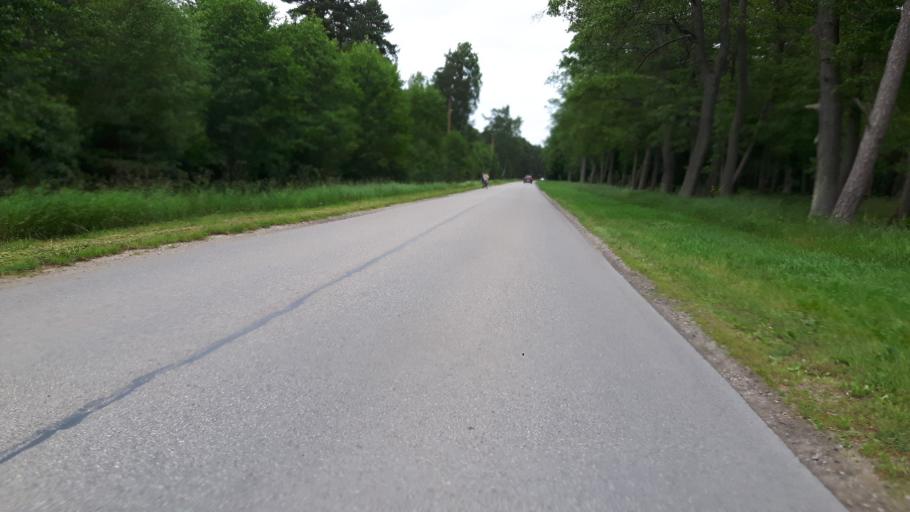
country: LV
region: Liepaja
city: Vec-Liepaja
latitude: 56.5646
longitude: 21.0150
